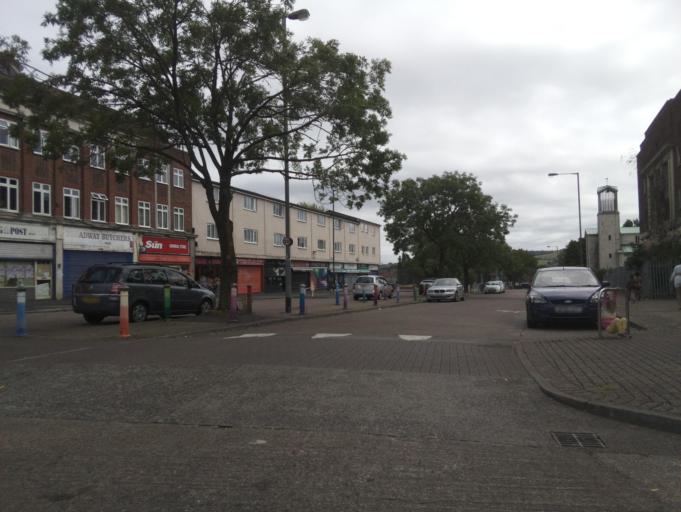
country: GB
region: England
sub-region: Bath and North East Somerset
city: Whitchurch
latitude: 51.4251
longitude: -2.5859
